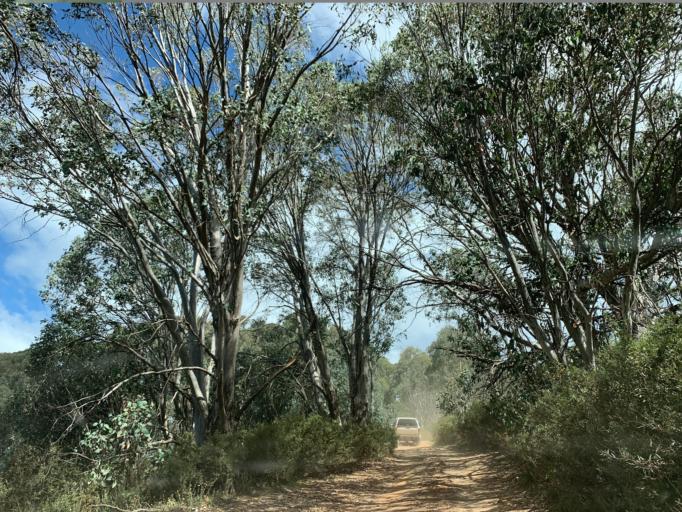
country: AU
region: Victoria
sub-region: Mansfield
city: Mansfield
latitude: -37.1096
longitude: 146.5335
